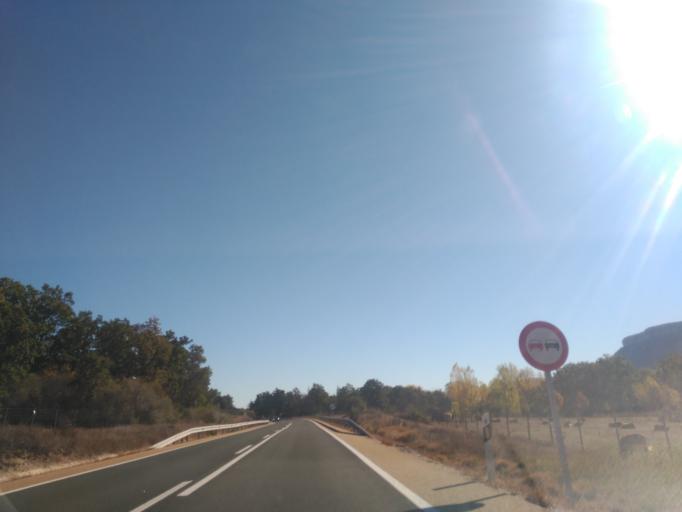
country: ES
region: Castille and Leon
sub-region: Provincia de Soria
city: Cidones
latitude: 41.8111
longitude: -2.6771
